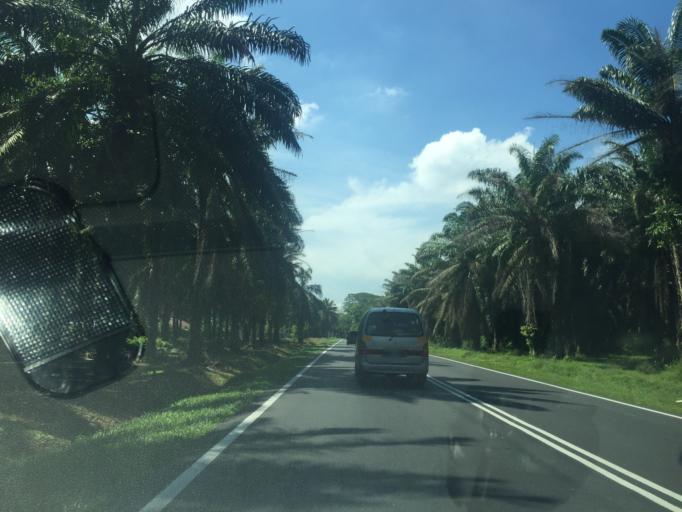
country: MY
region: Penang
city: Tasek Glugor
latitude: 5.5098
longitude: 100.5300
